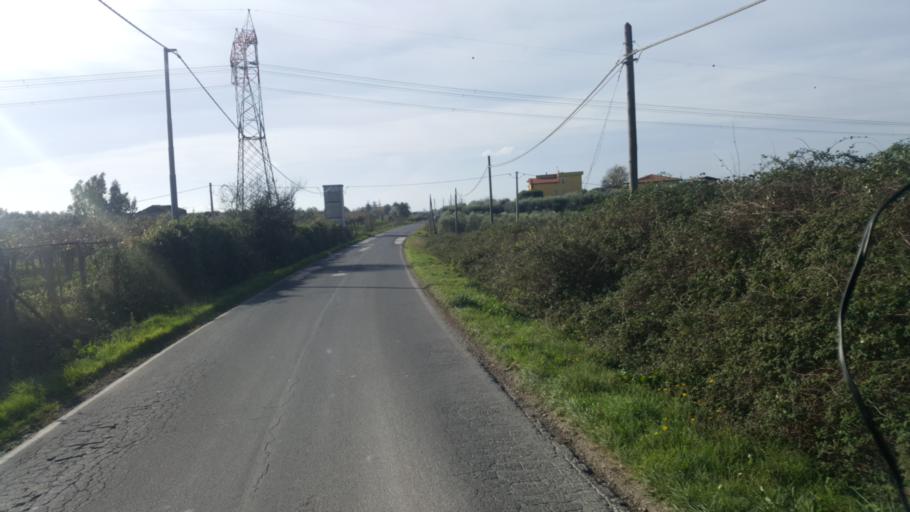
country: IT
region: Latium
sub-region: Provincia di Latina
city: Campoleone
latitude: 41.6422
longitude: 12.6199
